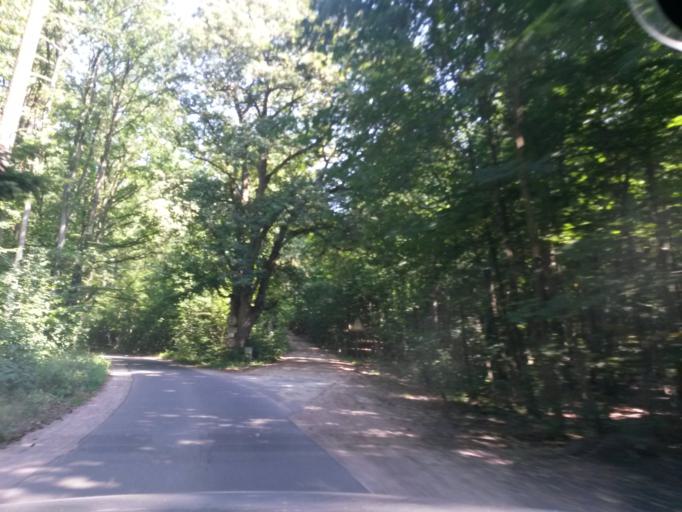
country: DE
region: Brandenburg
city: Marienwerder
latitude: 52.8904
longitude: 13.6427
